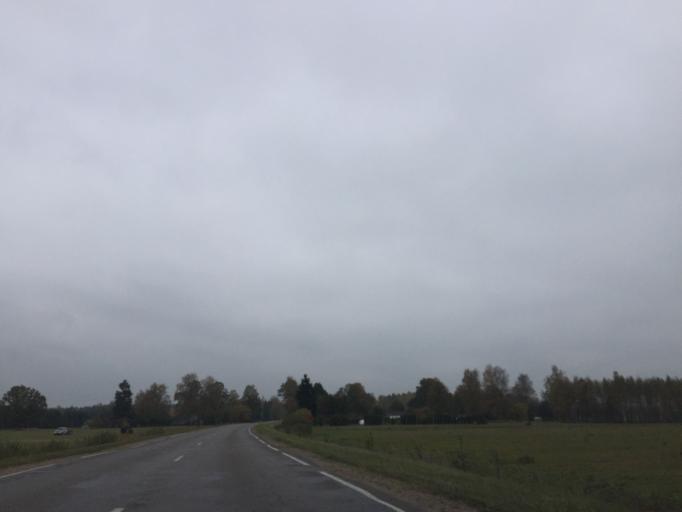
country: LV
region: Jelgava
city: Jelgava
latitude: 56.7288
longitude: 23.6827
